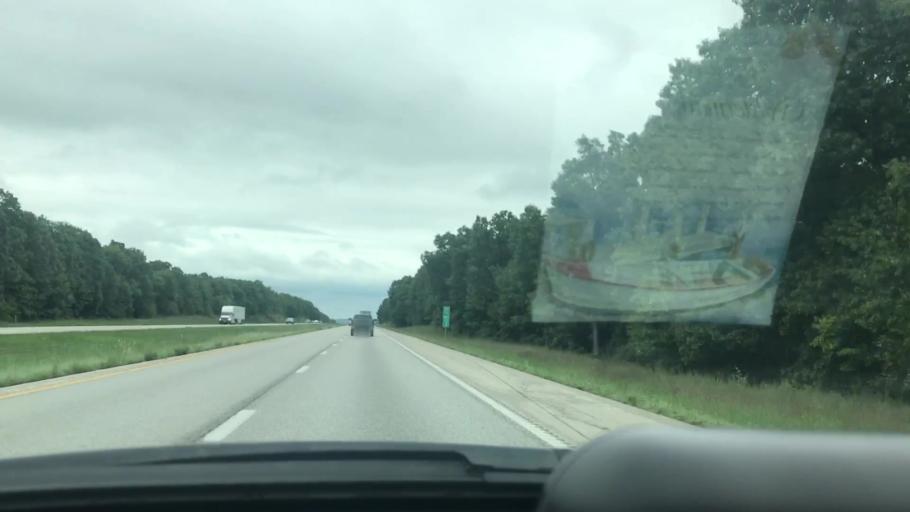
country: US
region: Missouri
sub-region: Lawrence County
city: Mount Vernon
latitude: 37.1421
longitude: -93.7174
